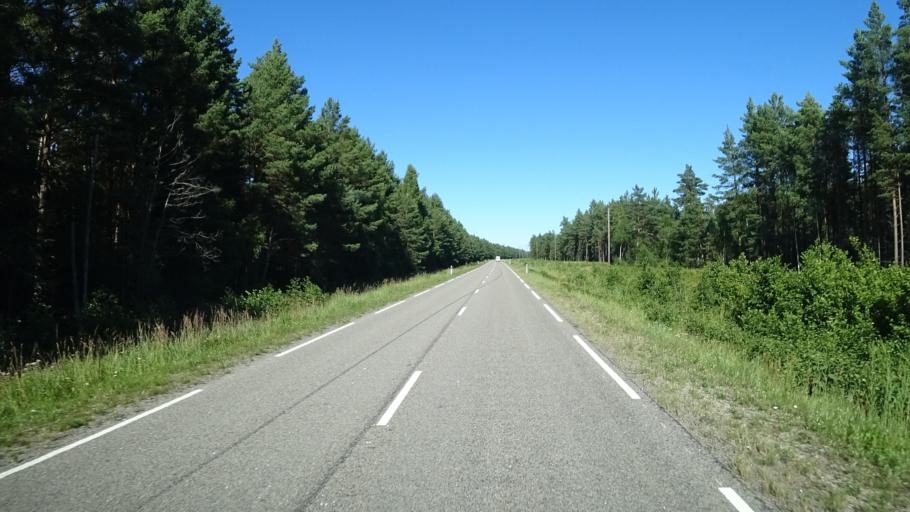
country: LV
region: Dundaga
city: Dundaga
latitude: 57.7138
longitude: 22.4567
